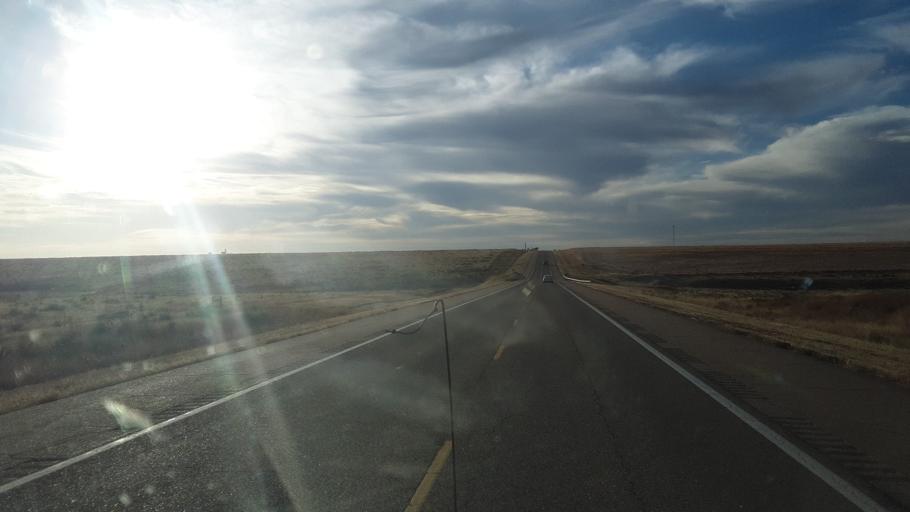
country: US
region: Kansas
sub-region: Hamilton County
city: Syracuse
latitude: 37.9440
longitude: -101.5199
